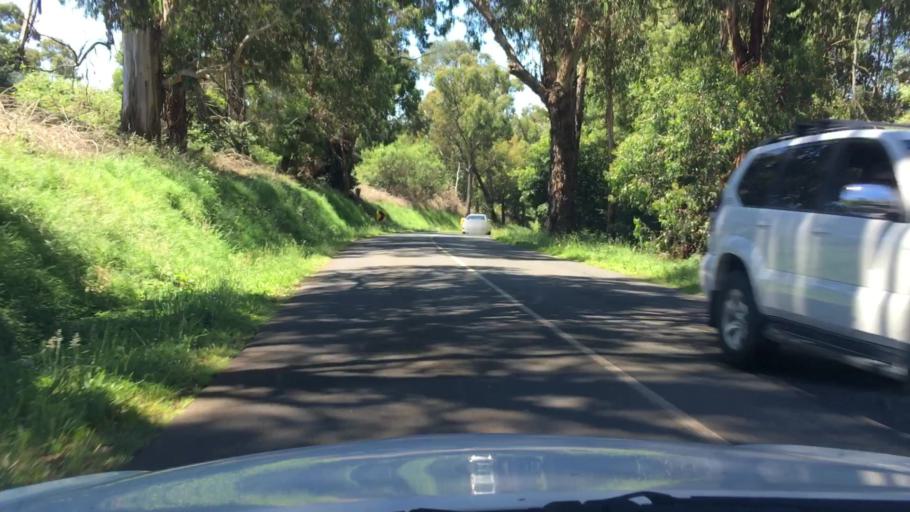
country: AU
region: Victoria
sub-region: Yarra Ranges
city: Mount Evelyn
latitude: -37.8063
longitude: 145.4087
